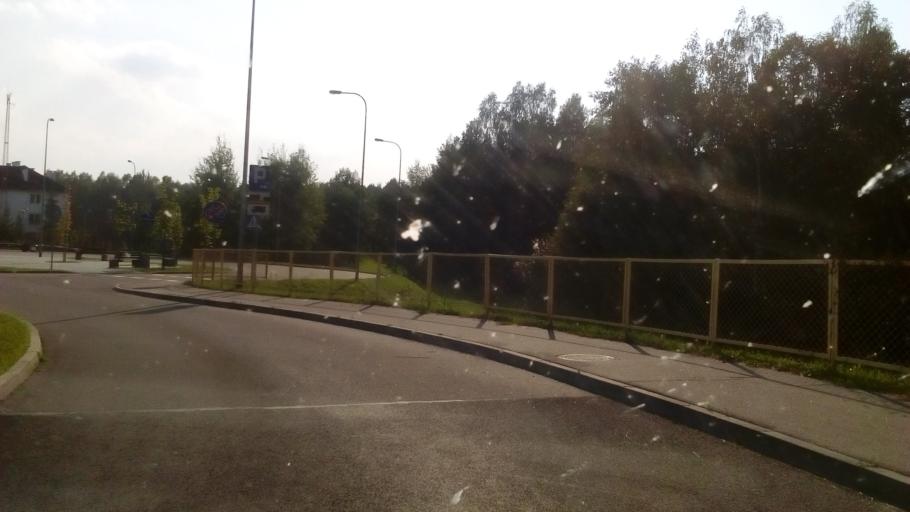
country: LT
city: Lazdijai
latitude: 54.1620
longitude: 23.4742
